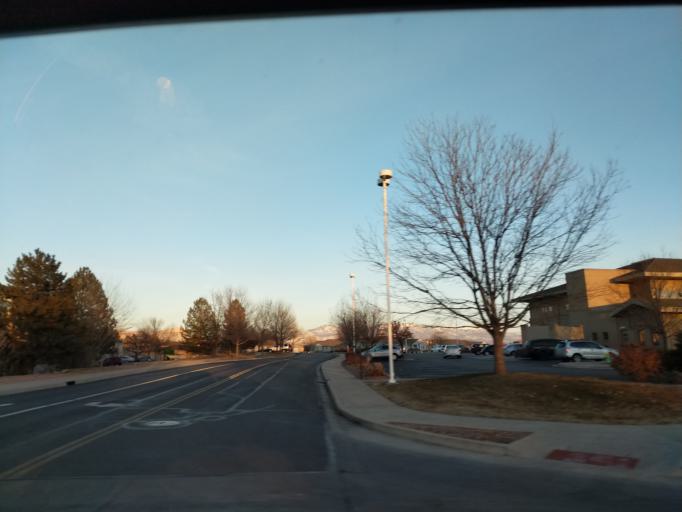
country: US
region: Colorado
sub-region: Mesa County
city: Grand Junction
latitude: 39.0970
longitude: -108.5523
